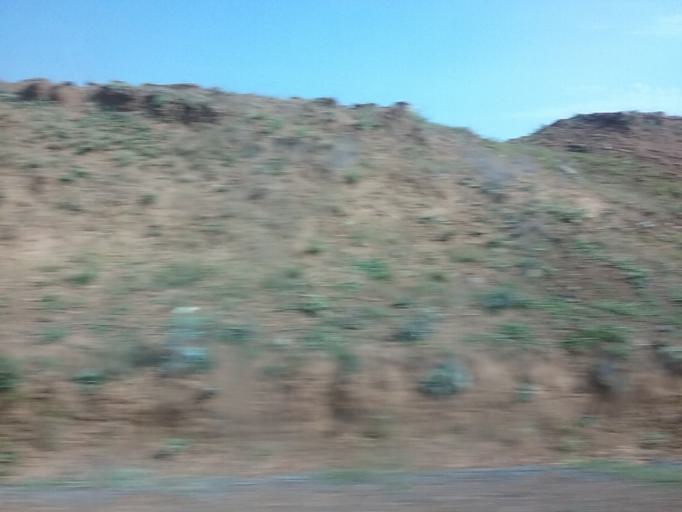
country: LS
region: Berea
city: Teyateyaneng
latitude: -29.0880
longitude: 27.9467
